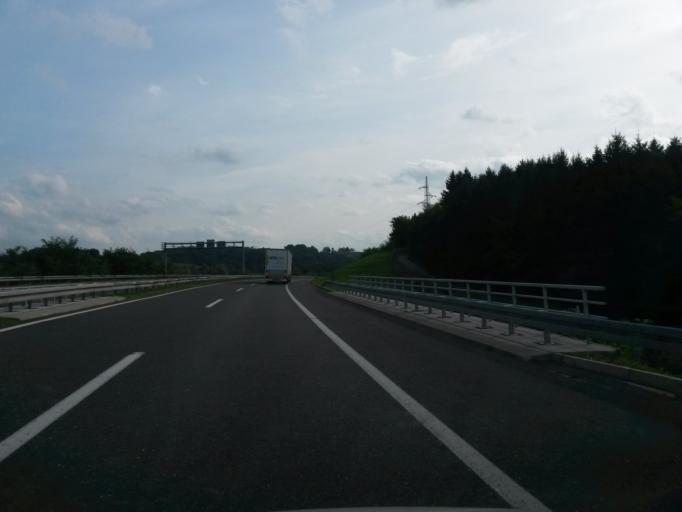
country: HR
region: Varazdinska
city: Jalzabet
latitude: 46.2502
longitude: 16.4001
